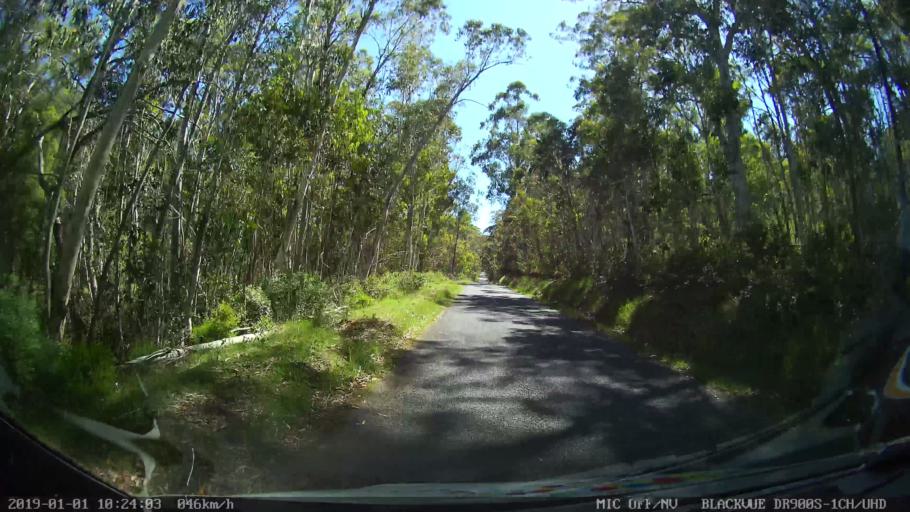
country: AU
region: New South Wales
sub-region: Snowy River
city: Jindabyne
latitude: -36.0737
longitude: 148.2166
